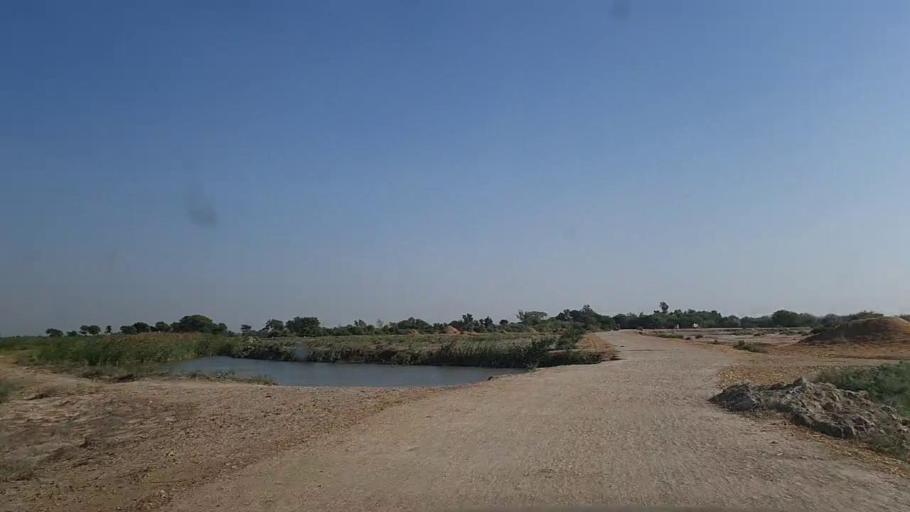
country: PK
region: Sindh
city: Daro Mehar
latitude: 24.6269
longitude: 68.0795
